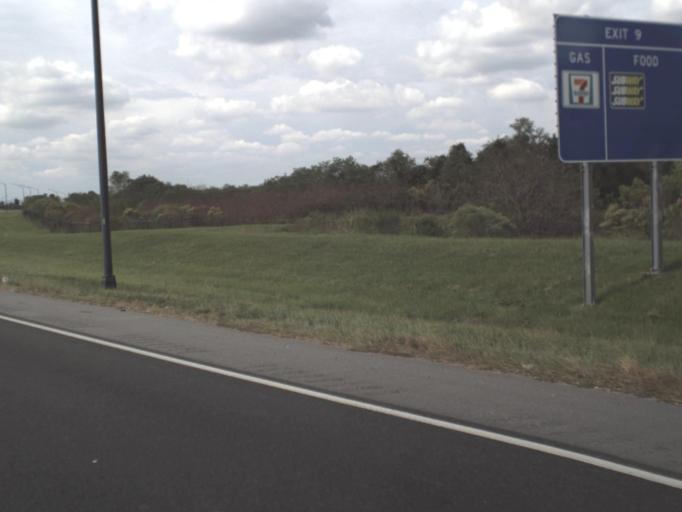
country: US
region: Florida
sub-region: Polk County
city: Crystal Lake
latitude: 27.9973
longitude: -81.9104
